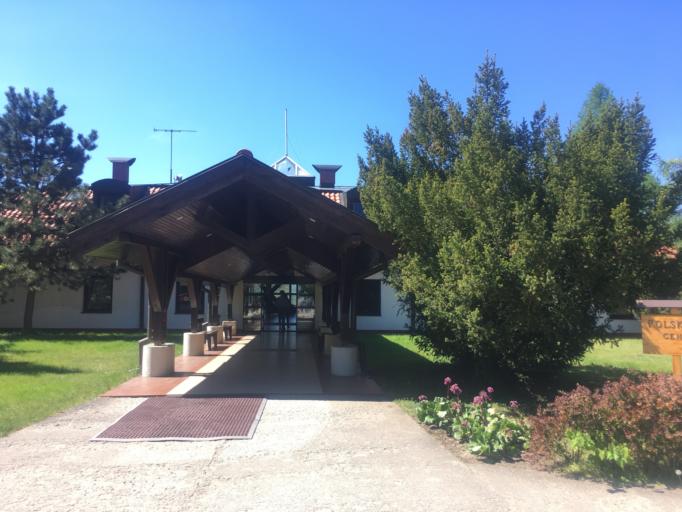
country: PL
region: Warmian-Masurian Voivodeship
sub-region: Powiat mragowski
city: Mikolajki
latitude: 53.7554
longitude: 21.6092
